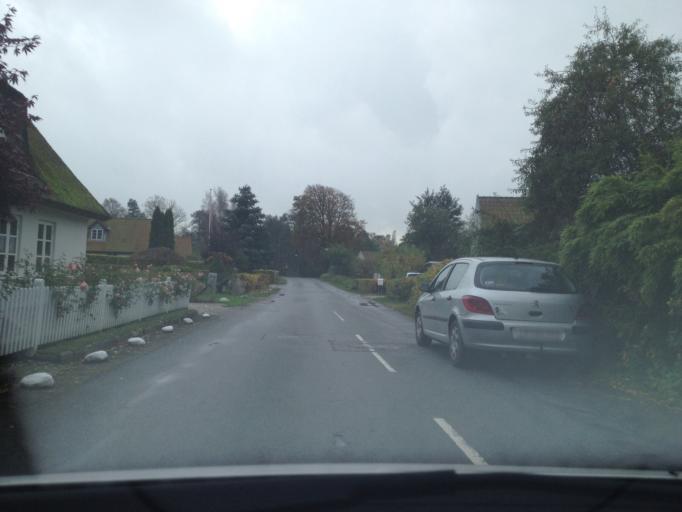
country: DK
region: Capital Region
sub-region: Hillerod Kommune
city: Nodebo
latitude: 55.9701
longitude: 12.3715
